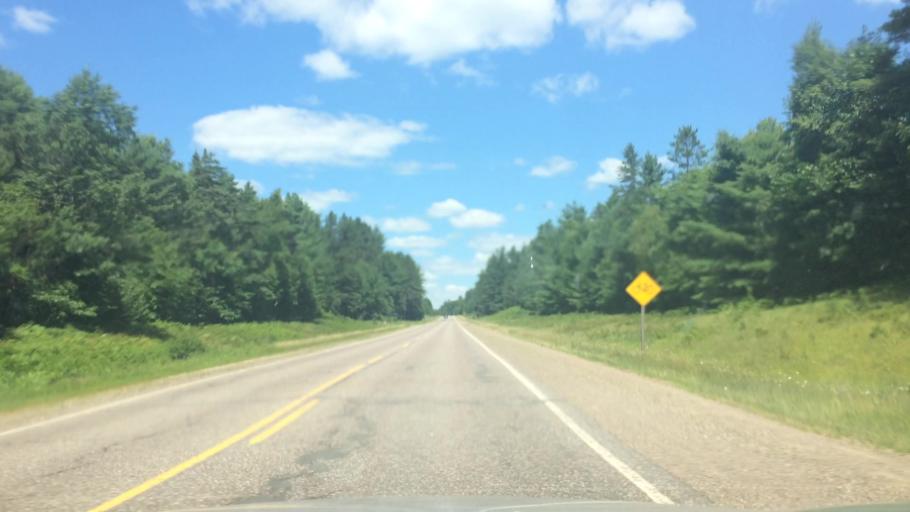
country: US
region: Wisconsin
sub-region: Vilas County
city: Lac du Flambeau
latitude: 46.0671
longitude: -89.6447
